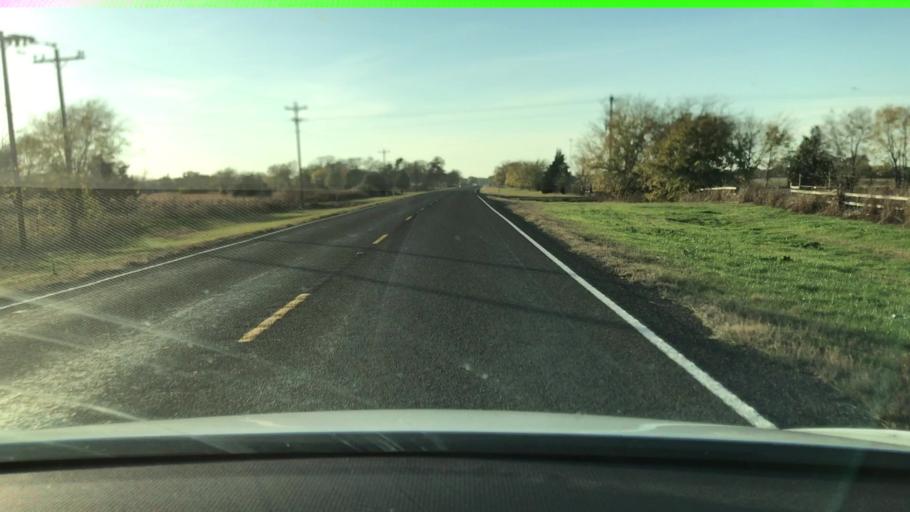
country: US
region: Texas
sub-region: Van Zandt County
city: Wills Point
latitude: 32.5699
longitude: -96.1092
